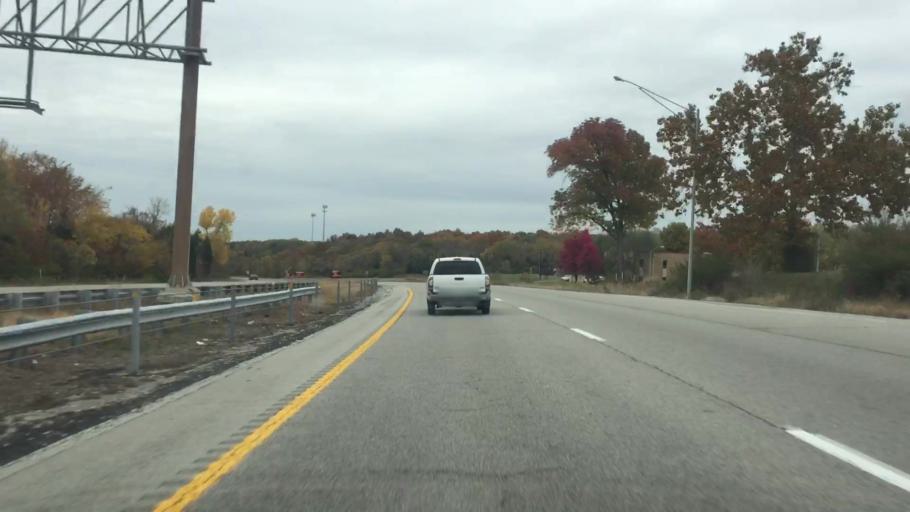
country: US
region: Missouri
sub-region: Jackson County
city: Lees Summit
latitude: 38.9478
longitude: -94.4101
